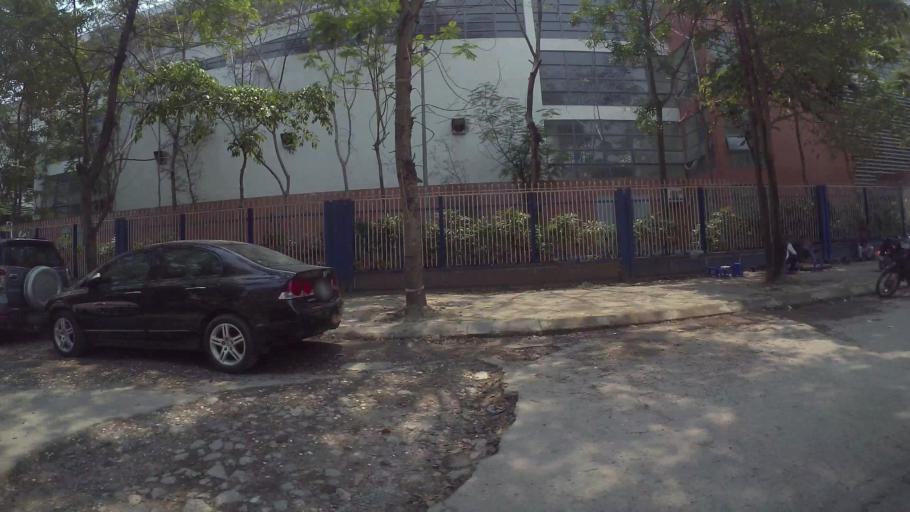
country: VN
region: Ha Noi
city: Thanh Xuan
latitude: 21.0081
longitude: 105.7991
